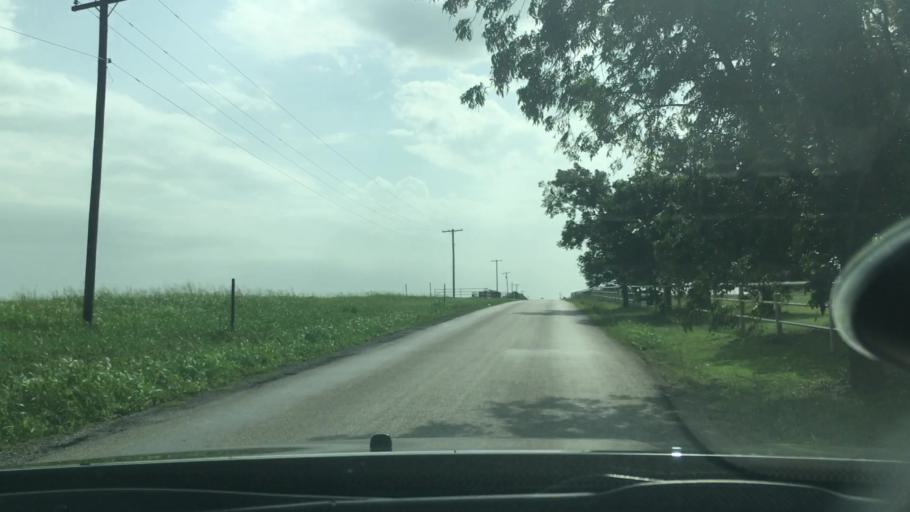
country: US
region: Oklahoma
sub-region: Carter County
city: Lone Grove
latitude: 34.2020
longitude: -97.2617
